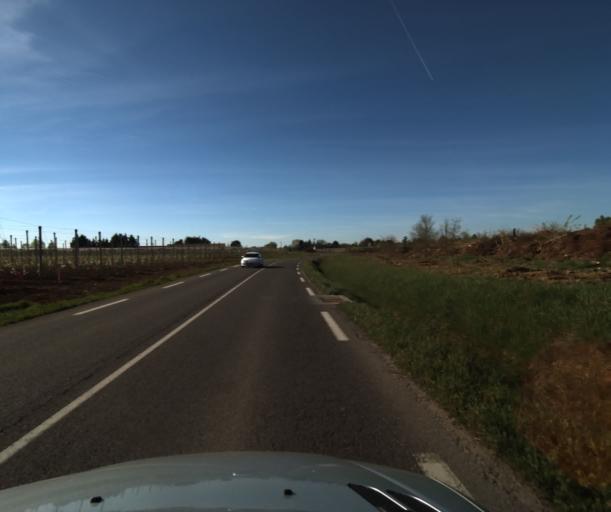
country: FR
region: Midi-Pyrenees
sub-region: Departement du Tarn-et-Garonne
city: Montbeton
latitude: 44.0355
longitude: 1.3117
